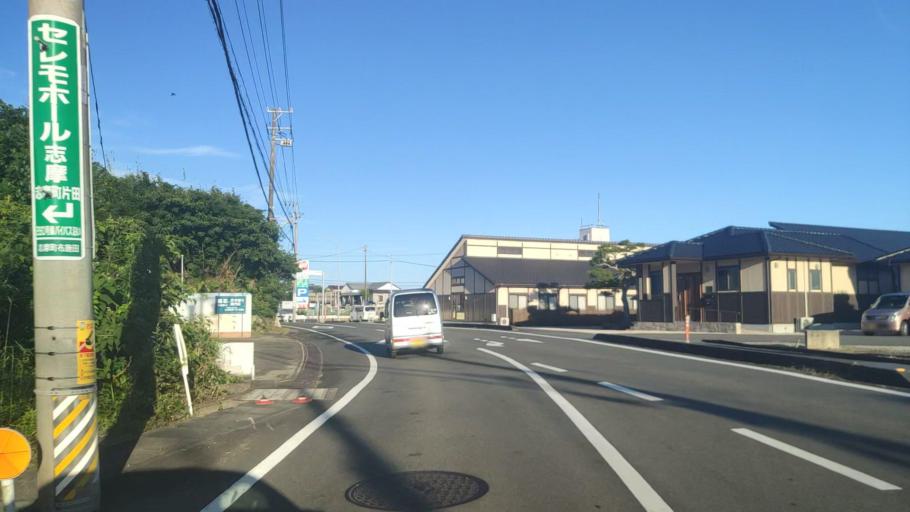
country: JP
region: Mie
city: Toba
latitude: 34.2557
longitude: 136.8239
